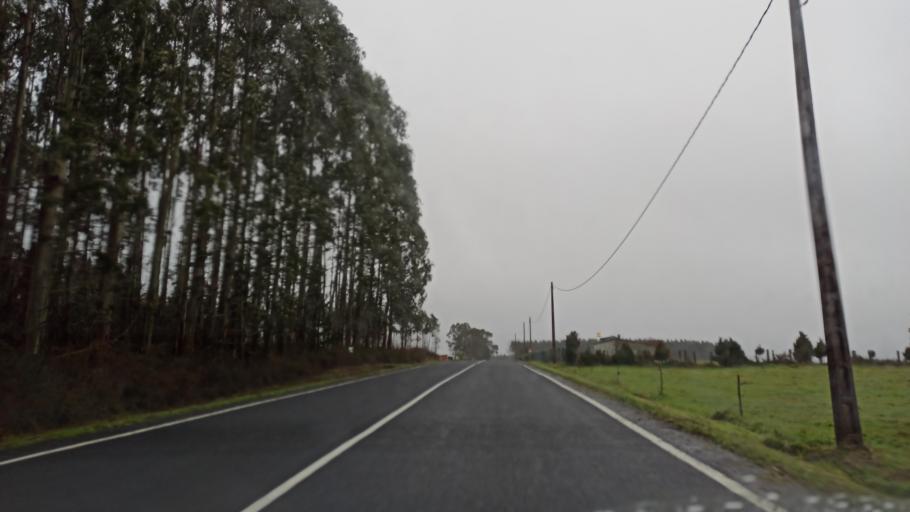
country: ES
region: Galicia
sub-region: Provincia da Coruna
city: Coiros
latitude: 43.1793
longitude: -8.1210
